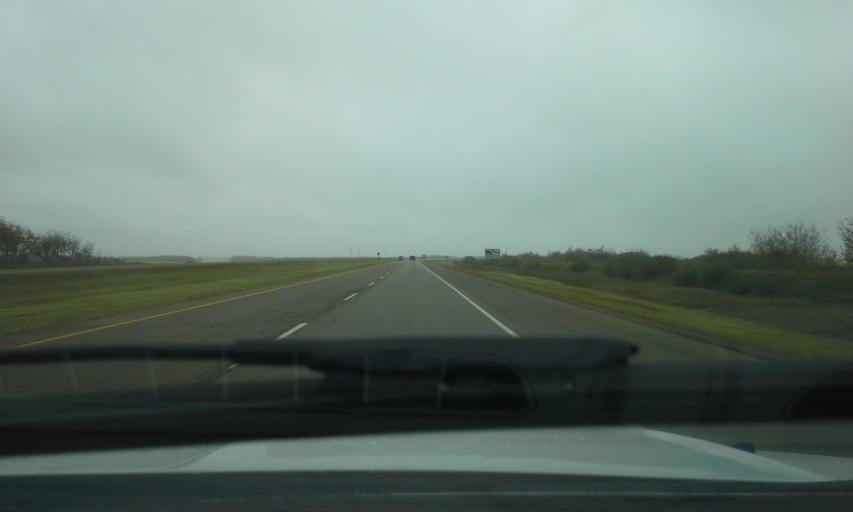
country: CA
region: Saskatchewan
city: Lloydminster
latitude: 53.2293
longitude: -109.8321
